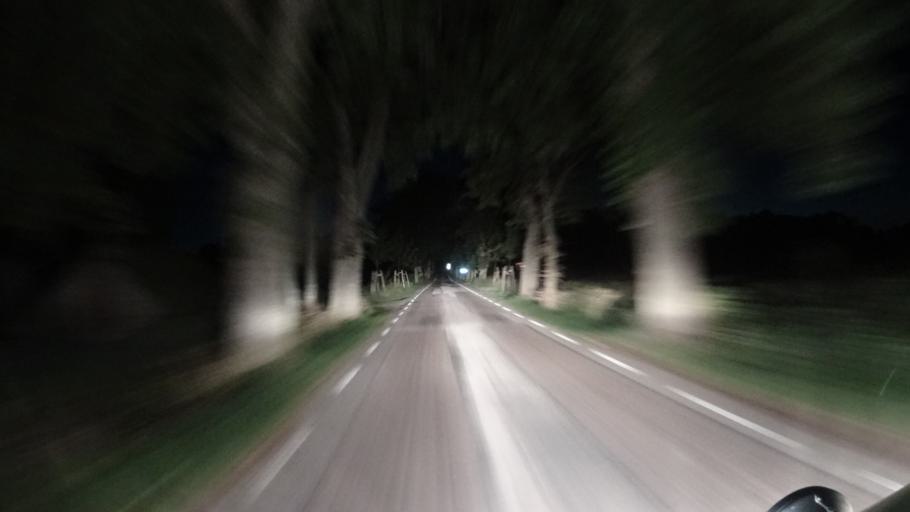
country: SE
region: OEstergoetland
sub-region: Vadstena Kommun
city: Herrestad
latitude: 58.3192
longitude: 14.8421
